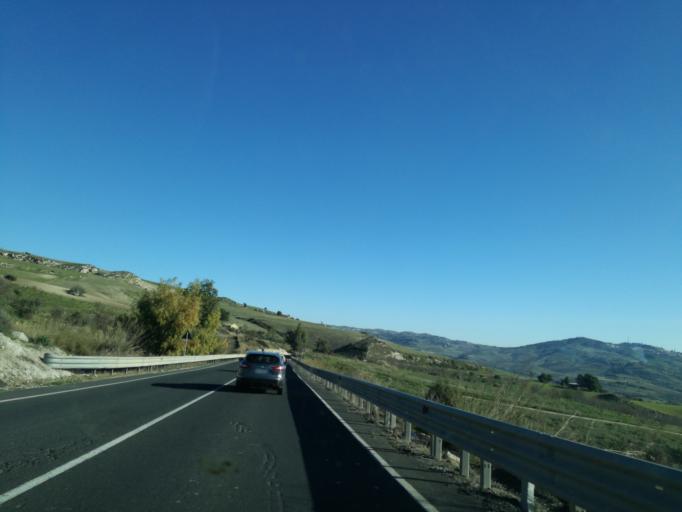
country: IT
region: Sicily
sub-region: Catania
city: San Michele di Ganzaria
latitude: 37.2281
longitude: 14.4383
